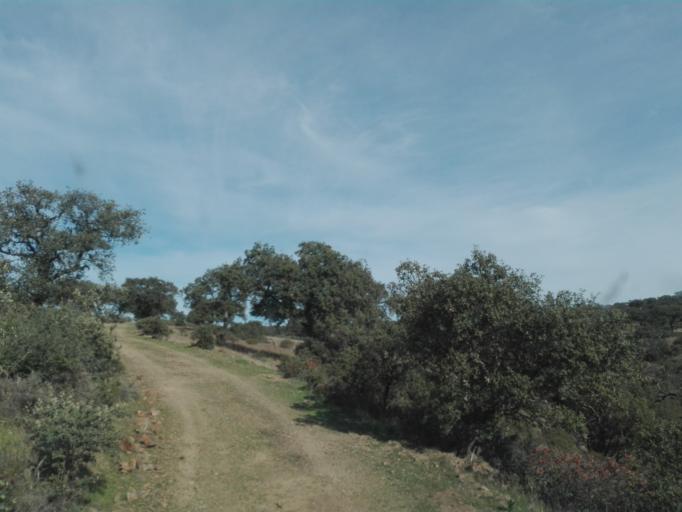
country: ES
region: Extremadura
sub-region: Provincia de Badajoz
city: Valverde de Llerena
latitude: 38.2125
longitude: -5.7466
